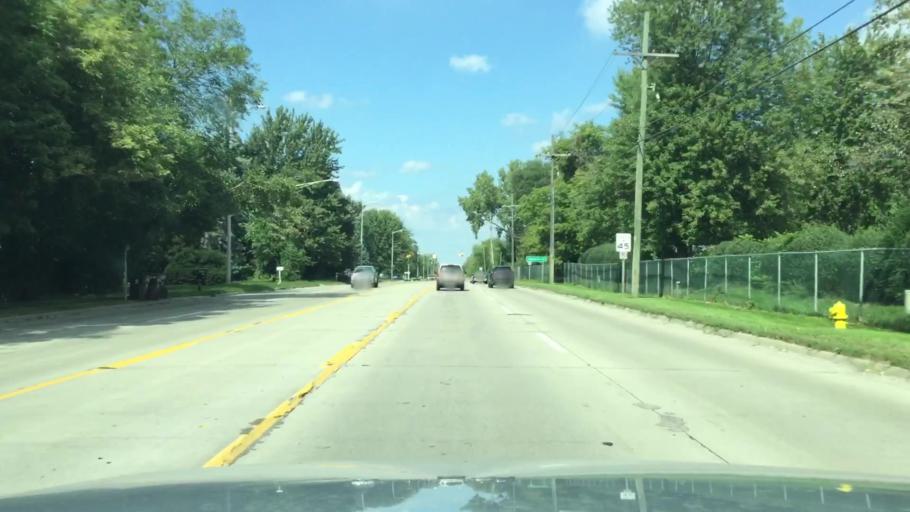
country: US
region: Michigan
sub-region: Wayne County
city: Wayne
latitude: 42.2730
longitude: -83.3481
